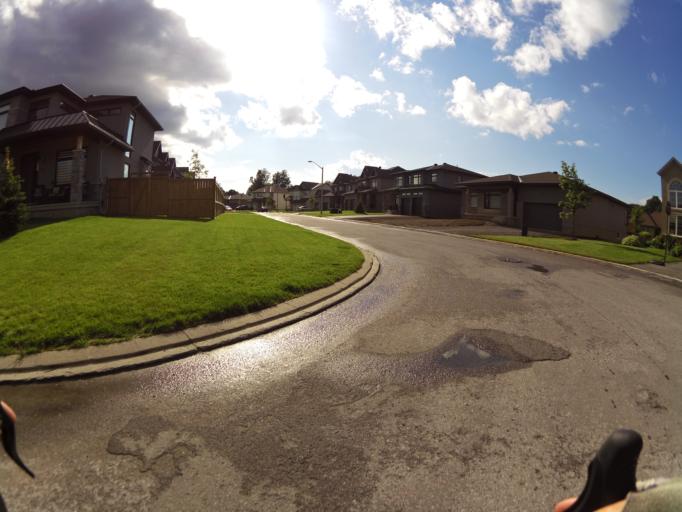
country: CA
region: Ontario
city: Bells Corners
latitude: 45.2009
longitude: -75.8375
